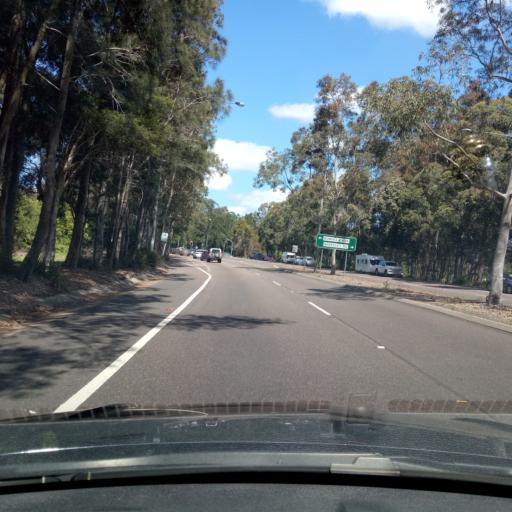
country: AU
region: New South Wales
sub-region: Wyong Shire
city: Berkeley Vale
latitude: -33.3399
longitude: 151.4288
